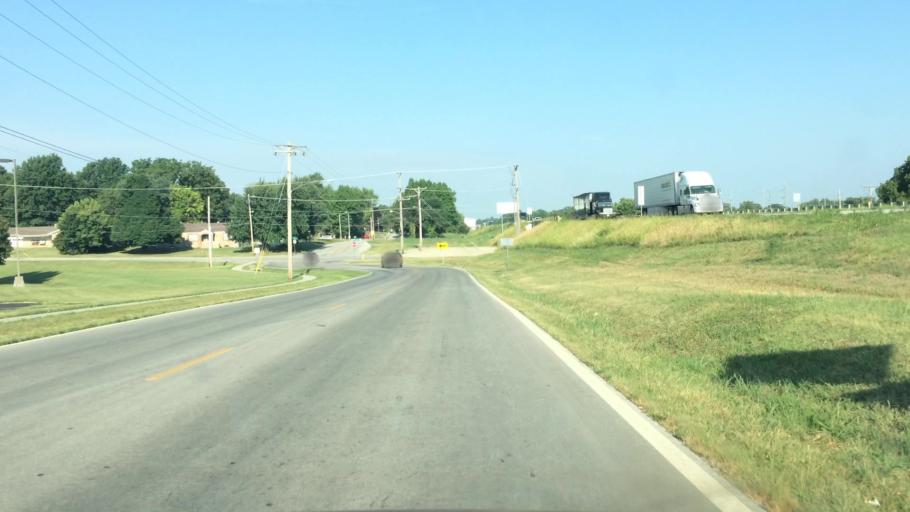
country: US
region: Missouri
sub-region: Greene County
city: Springfield
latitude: 37.2500
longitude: -93.2727
